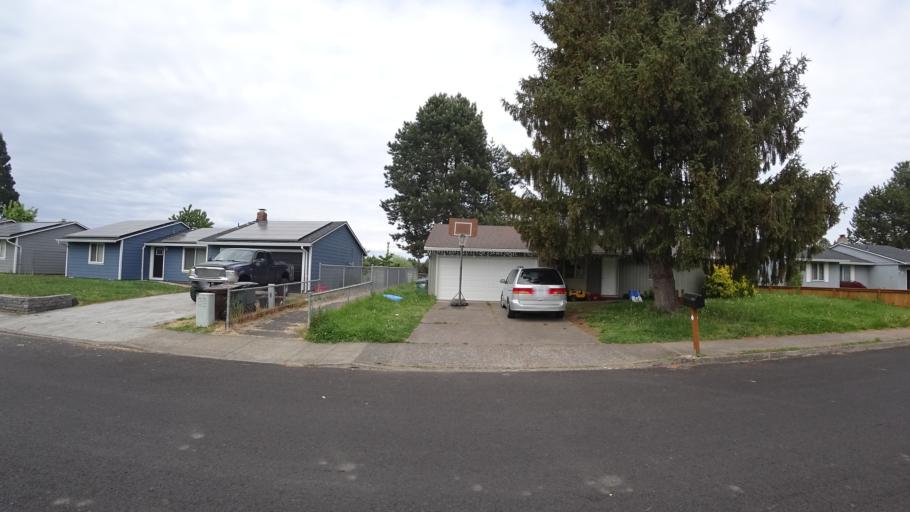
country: US
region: Oregon
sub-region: Washington County
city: Hillsboro
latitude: 45.4941
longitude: -122.9629
